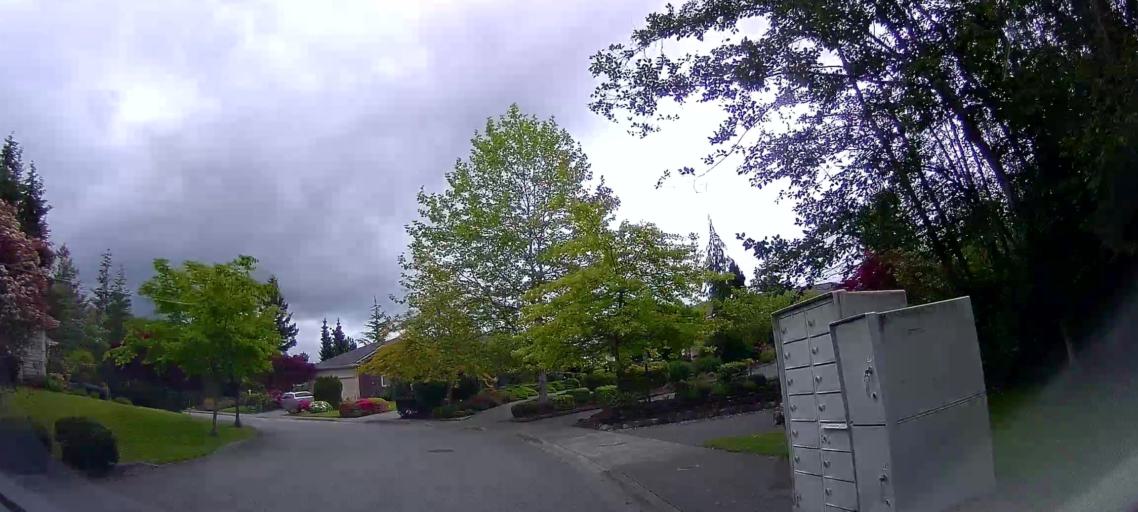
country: US
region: Washington
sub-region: Skagit County
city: Big Lake
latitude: 48.4133
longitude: -122.2852
